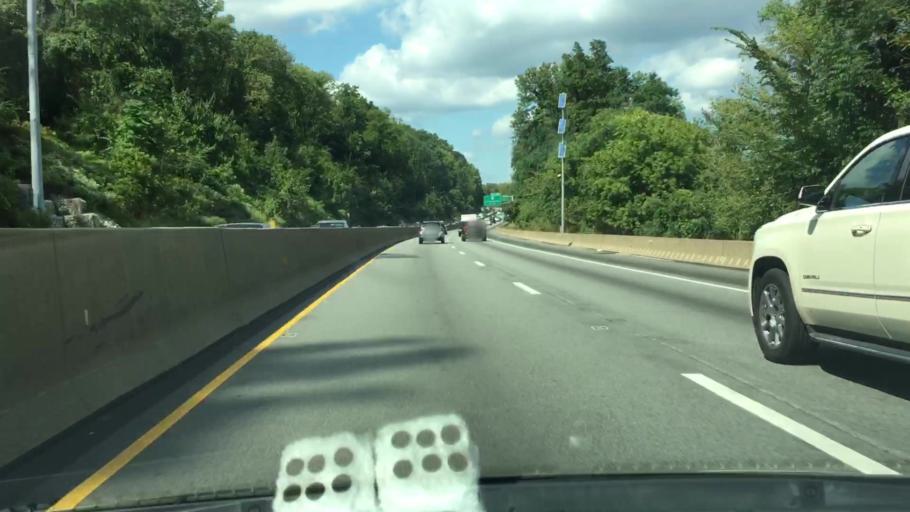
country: US
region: Pennsylvania
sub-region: Montgomery County
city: Conshohocken
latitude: 40.0636
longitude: -75.2762
